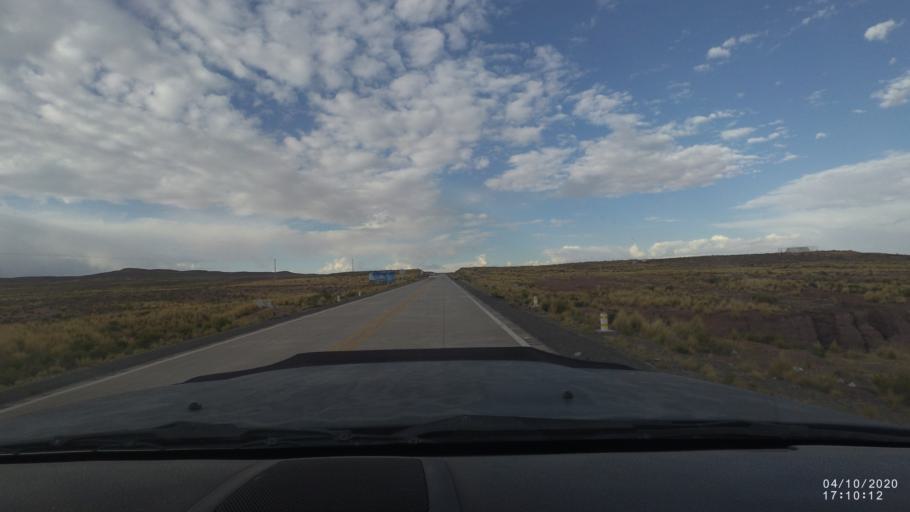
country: BO
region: Oruro
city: Oruro
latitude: -18.3342
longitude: -67.5863
